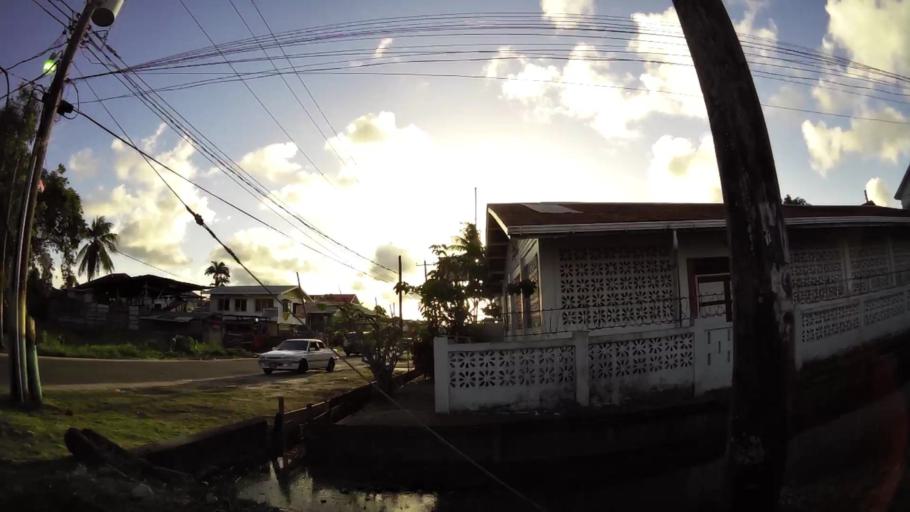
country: GY
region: Demerara-Mahaica
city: Georgetown
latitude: 6.8014
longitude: -58.1501
